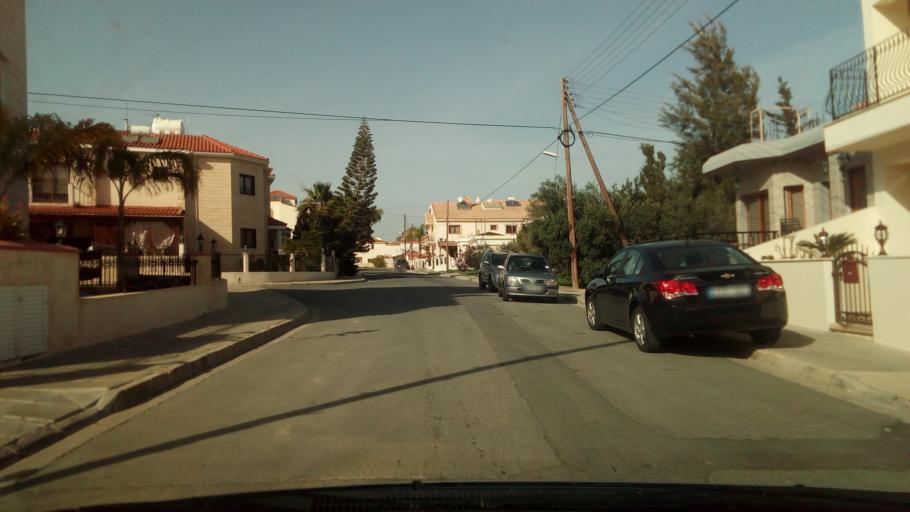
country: CY
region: Larnaka
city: Dhromolaxia
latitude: 34.9056
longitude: 33.5910
